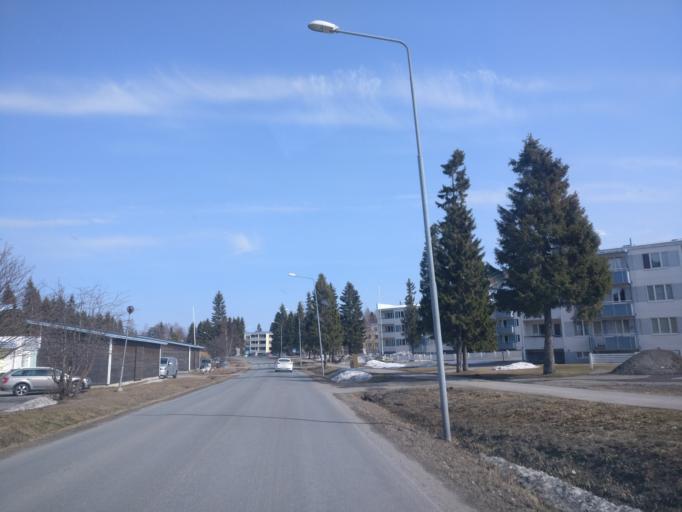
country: FI
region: Lapland
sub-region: Kemi-Tornio
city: Kemi
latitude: 65.7273
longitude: 24.6239
